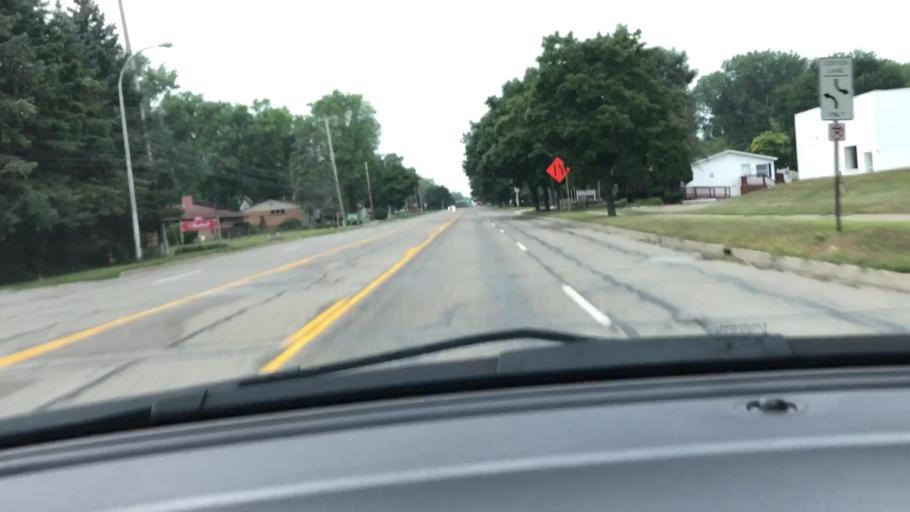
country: US
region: Michigan
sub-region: Midland County
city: Midland
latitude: 43.6050
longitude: -84.1799
